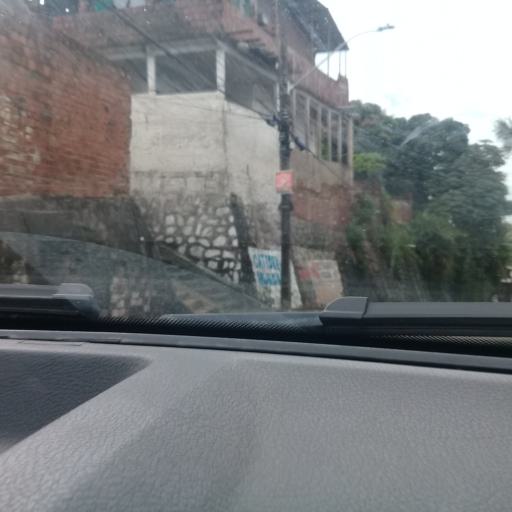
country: BR
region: Pernambuco
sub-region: Jaboatao Dos Guararapes
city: Jaboatao dos Guararapes
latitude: -8.1114
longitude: -34.9539
